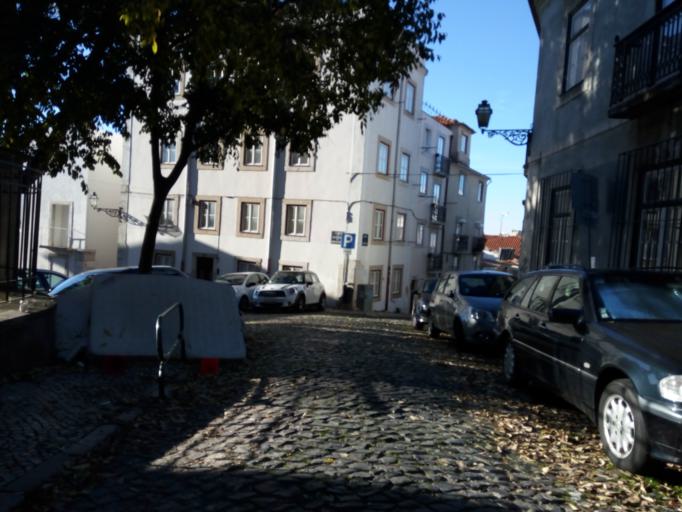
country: PT
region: Lisbon
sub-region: Lisbon
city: Lisbon
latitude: 38.7139
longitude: -9.1271
